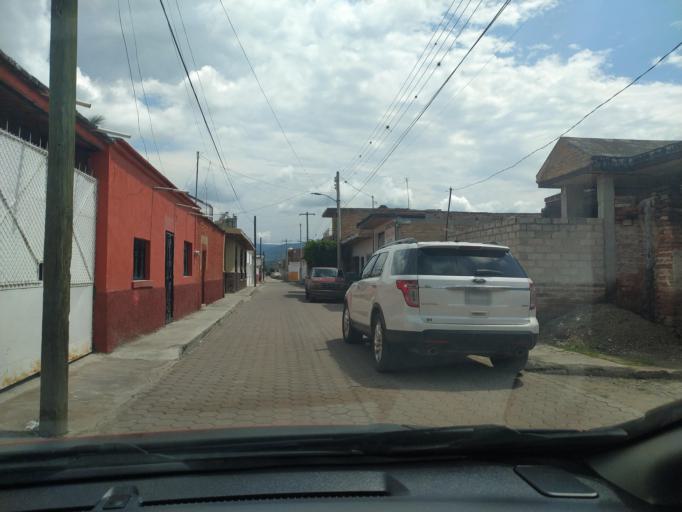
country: MX
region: Jalisco
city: Villa Corona
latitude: 20.3505
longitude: -103.6720
